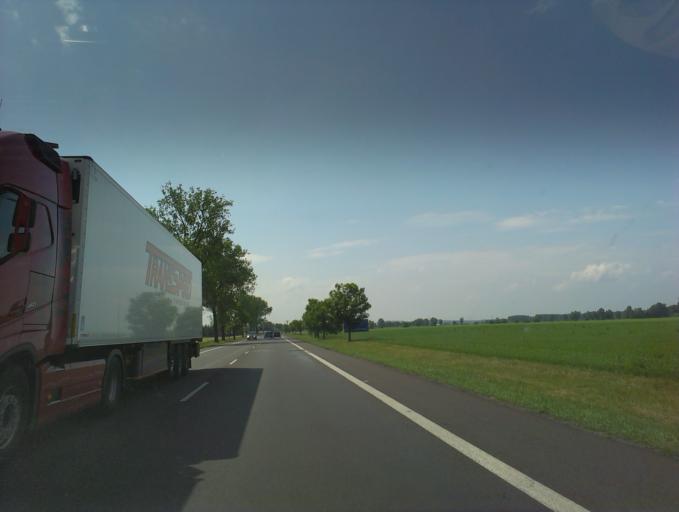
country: PL
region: Greater Poland Voivodeship
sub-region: Powiat pilski
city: Pila
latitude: 53.1057
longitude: 16.7484
